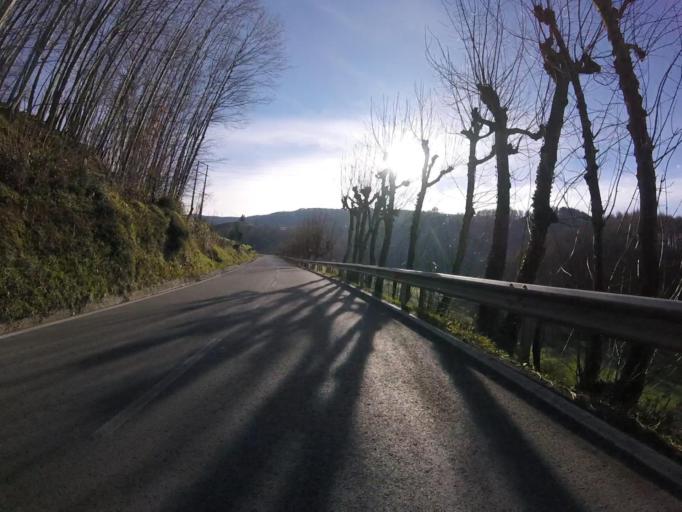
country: ES
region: Navarre
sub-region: Provincia de Navarra
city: Leitza
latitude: 43.0865
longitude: -1.9051
